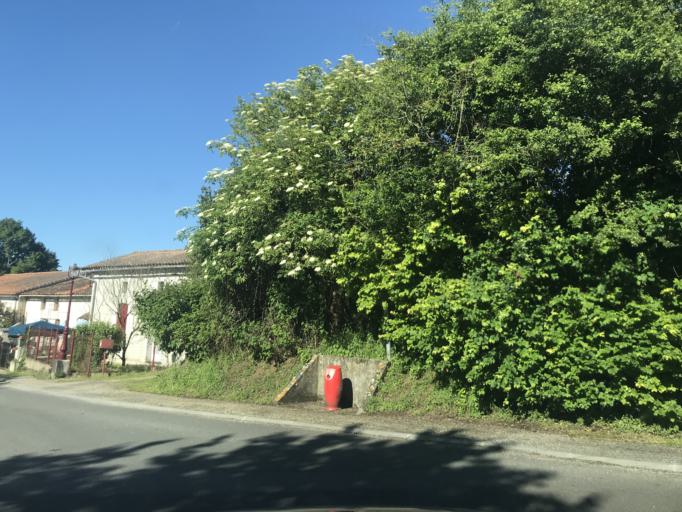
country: FR
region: Poitou-Charentes
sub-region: Departement de la Charente
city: Chalais
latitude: 45.2470
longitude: 0.0028
